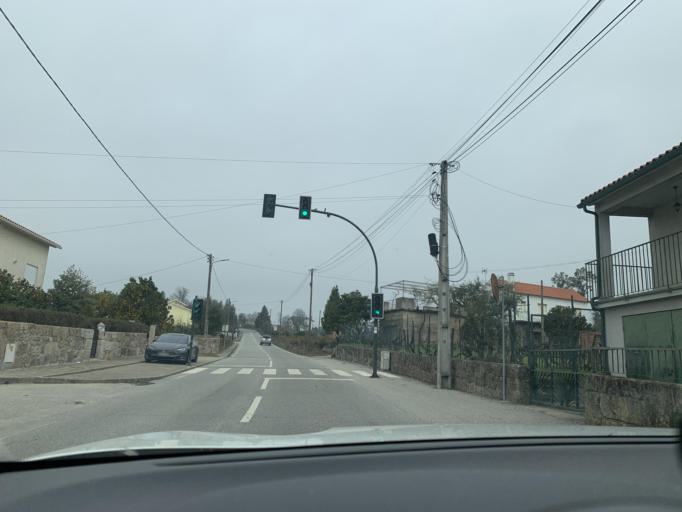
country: PT
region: Viseu
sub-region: Concelho de Tondela
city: Tondela
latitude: 40.5004
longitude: -8.0758
